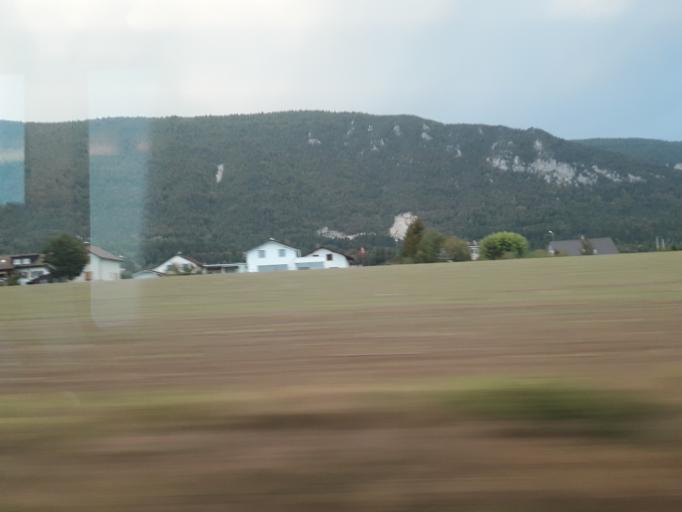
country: CH
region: Solothurn
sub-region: Bezirk Lebern
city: Selzach
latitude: 47.2190
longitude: 7.4750
